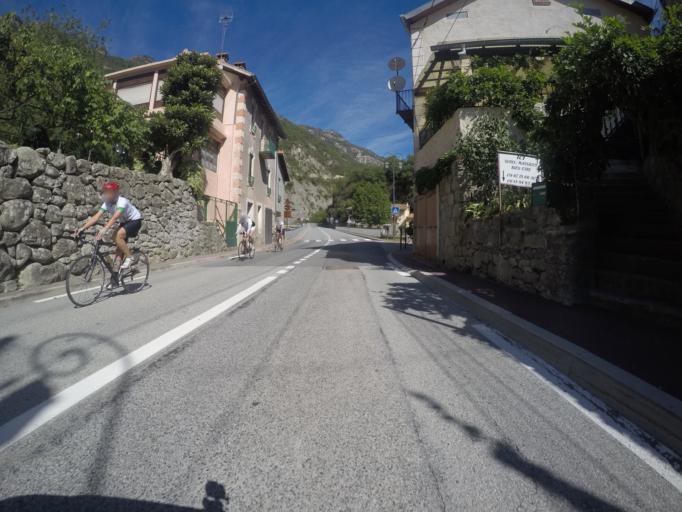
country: FR
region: Provence-Alpes-Cote d'Azur
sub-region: Departement des Alpes-Maritimes
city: Gilette
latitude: 43.9743
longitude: 7.1408
